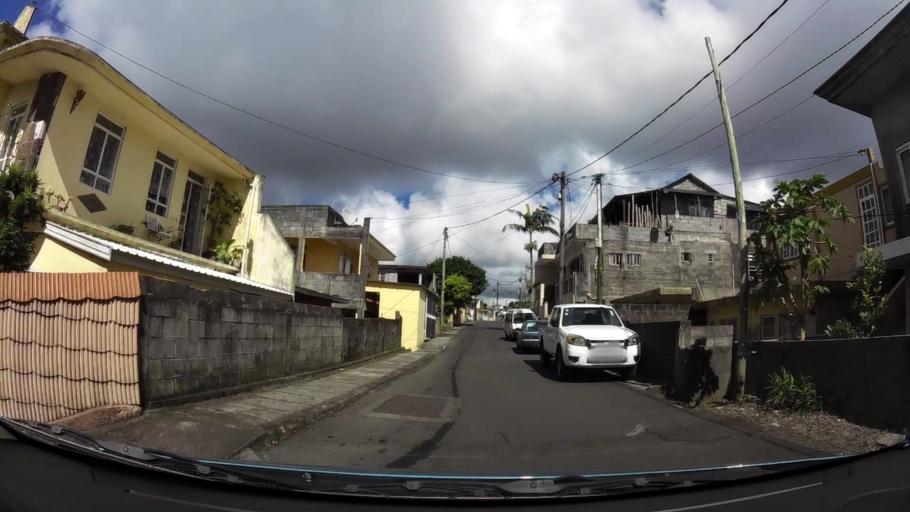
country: MU
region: Plaines Wilhems
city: Curepipe
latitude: -20.3317
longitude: 57.5252
